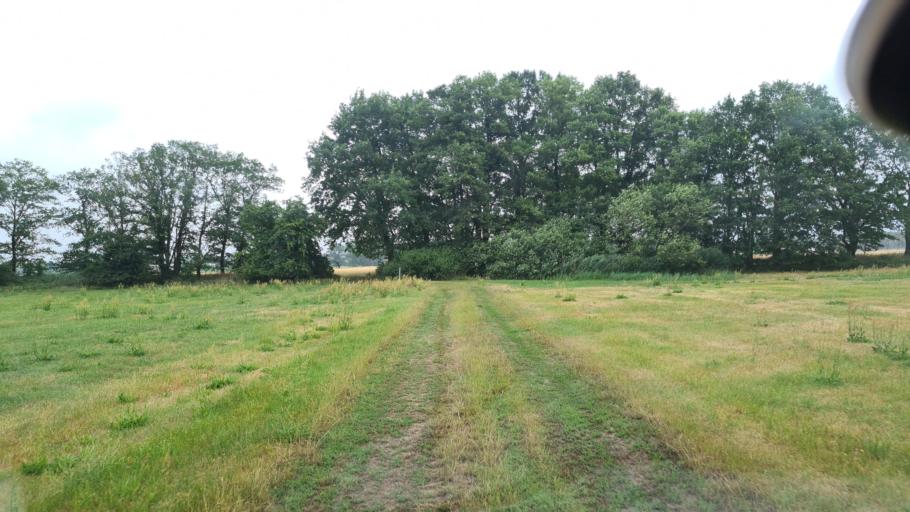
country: DE
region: Brandenburg
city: Herzberg
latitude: 51.7300
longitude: 13.2019
